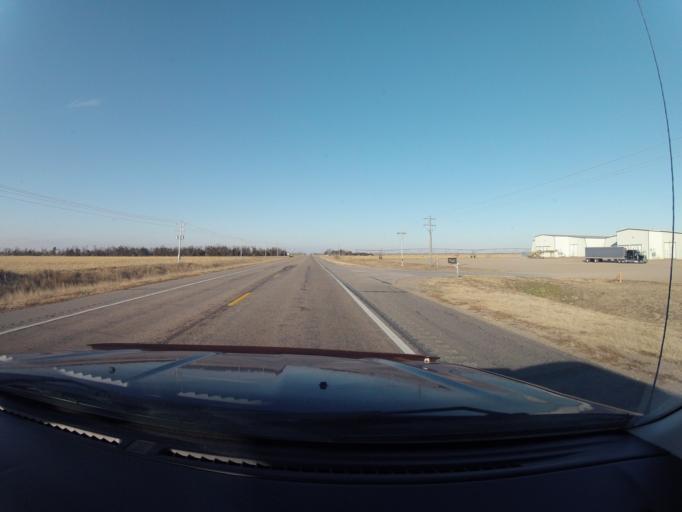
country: US
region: Nebraska
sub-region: Kearney County
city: Minden
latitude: 40.6286
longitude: -98.9514
